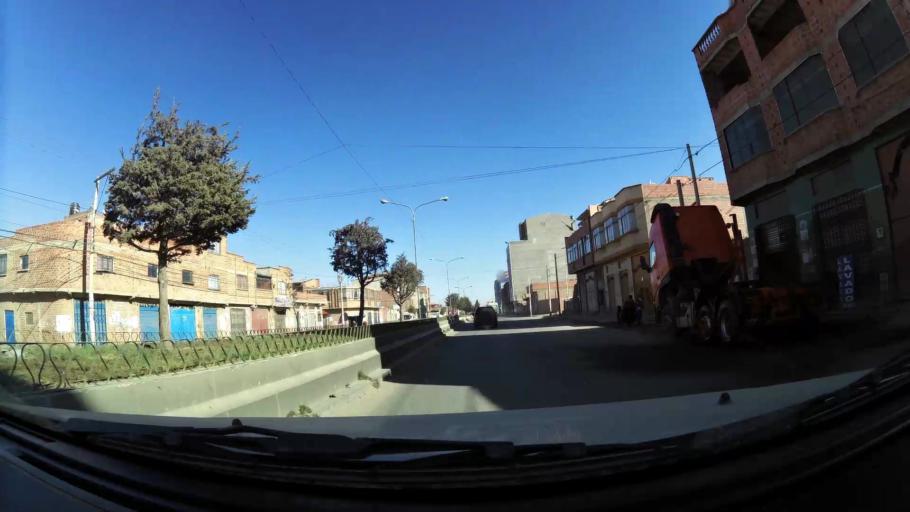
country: BO
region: La Paz
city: La Paz
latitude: -16.5401
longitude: -68.1830
